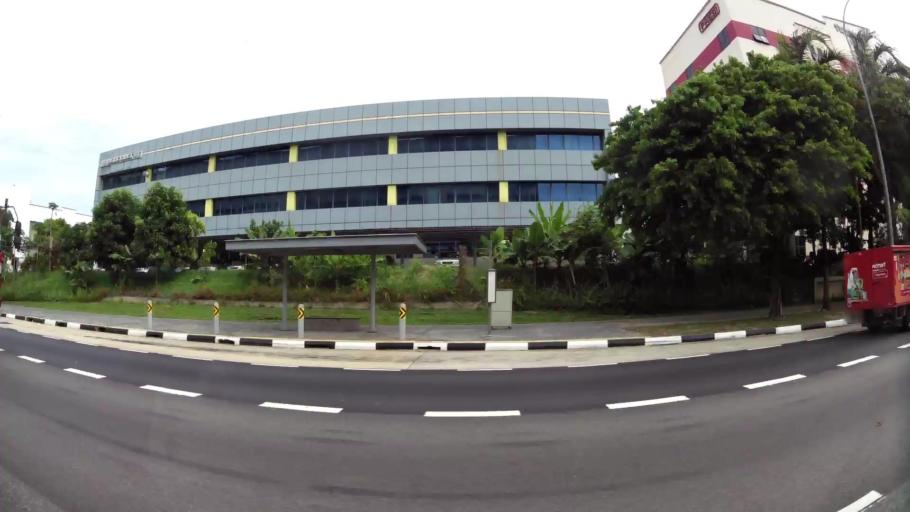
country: SG
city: Singapore
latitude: 1.3122
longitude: 103.7305
